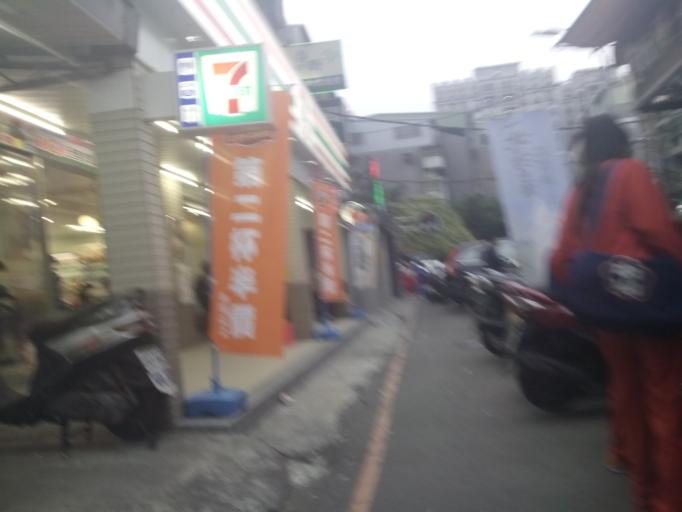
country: TW
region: Taipei
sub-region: Taipei
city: Banqiao
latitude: 25.0191
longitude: 121.4668
